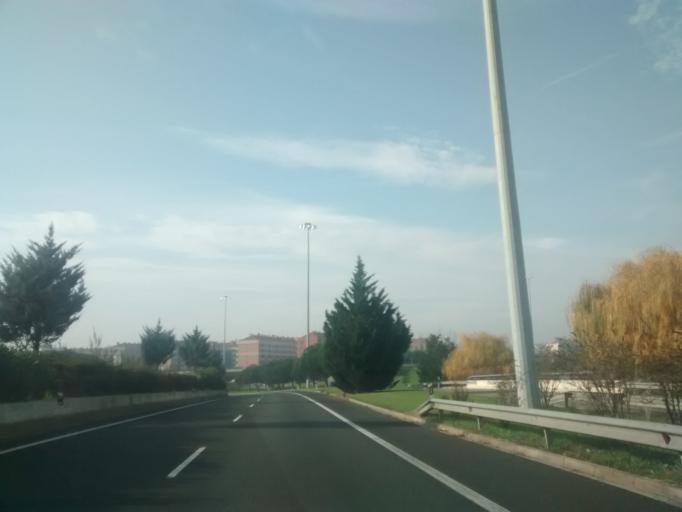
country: ES
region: La Rioja
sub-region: Provincia de La Rioja
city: Logrono
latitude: 42.4565
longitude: -2.4233
